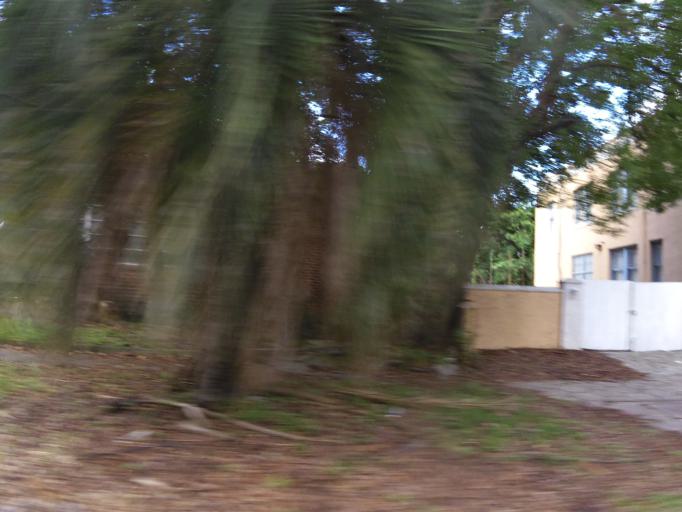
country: US
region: Florida
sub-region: Duval County
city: Jacksonville
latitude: 30.3126
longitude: -81.6927
